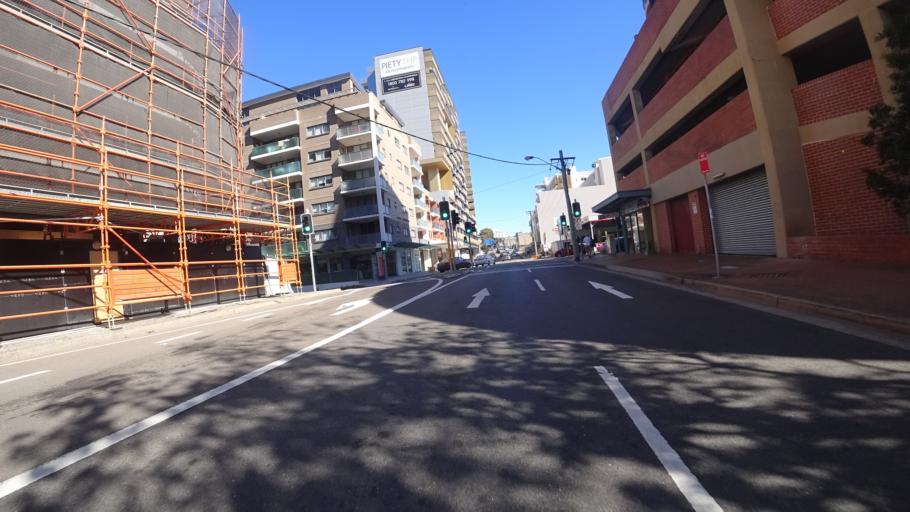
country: AU
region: New South Wales
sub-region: Kogarah
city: Kogarah Bay
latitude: -33.9678
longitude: 151.1087
